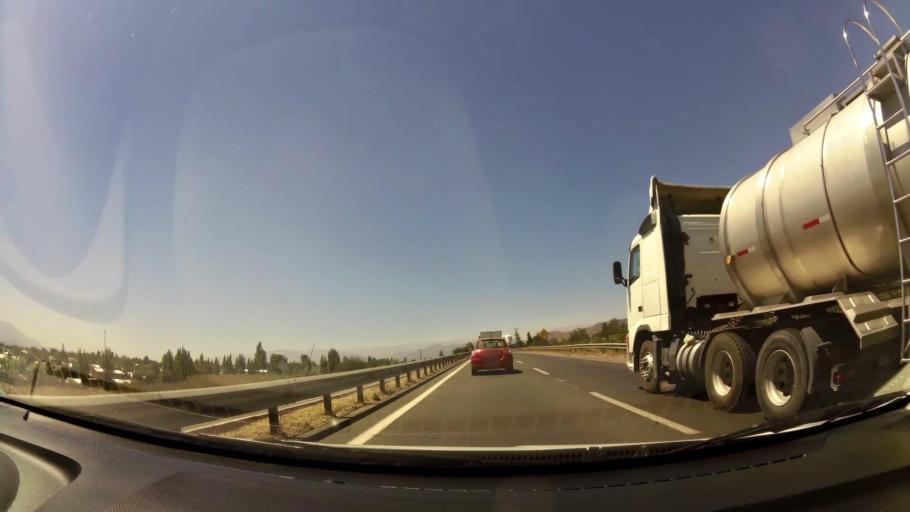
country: CL
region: O'Higgins
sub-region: Provincia de Cachapoal
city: Rancagua
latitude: -34.2322
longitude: -70.7889
